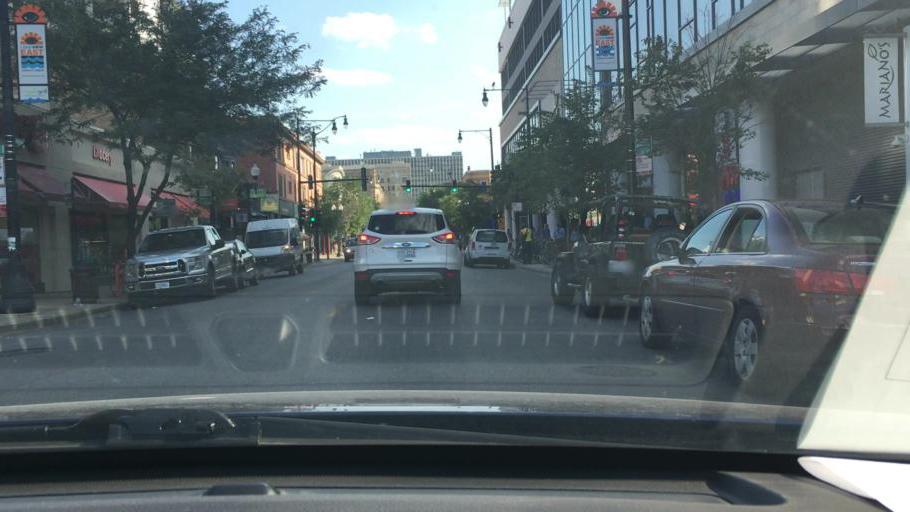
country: US
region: Illinois
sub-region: Cook County
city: Chicago
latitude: 41.9377
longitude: -87.6443
